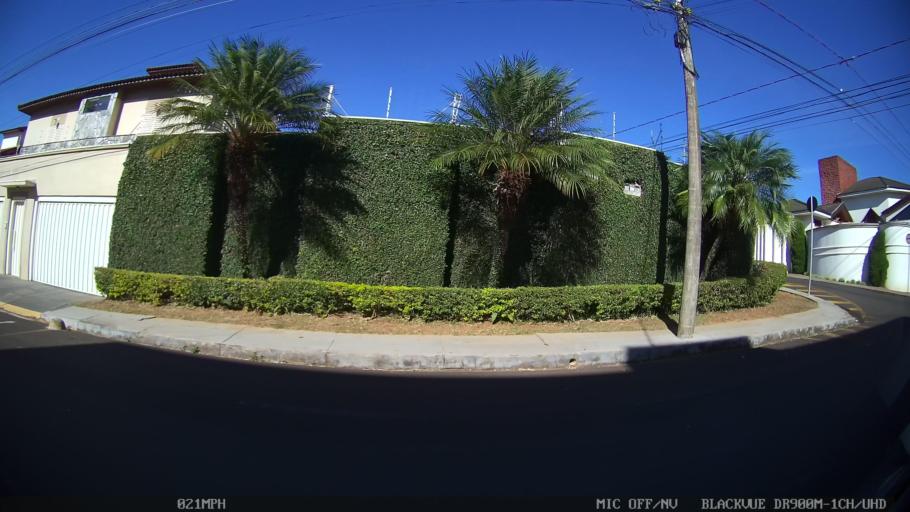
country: BR
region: Sao Paulo
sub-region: Franca
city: Franca
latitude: -20.5309
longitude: -47.4099
